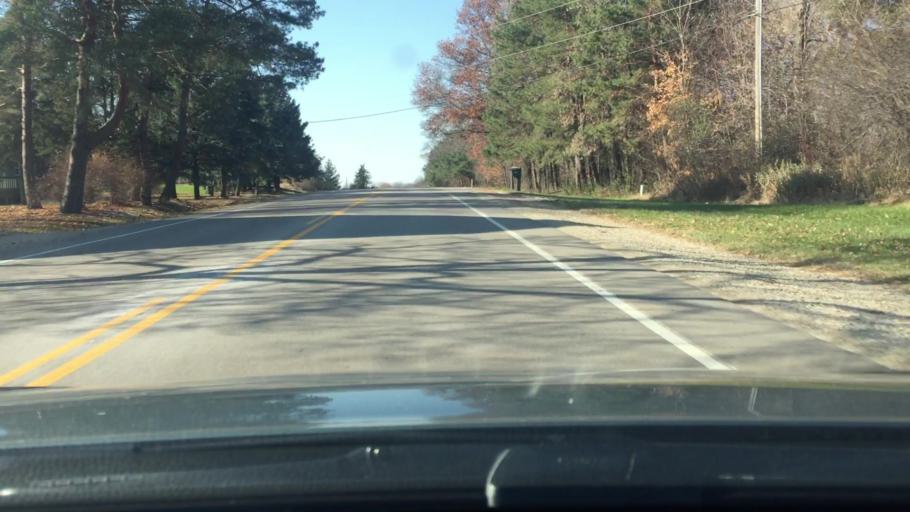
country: US
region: Wisconsin
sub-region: Jefferson County
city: Lake Ripley
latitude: 43.0120
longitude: -88.9831
